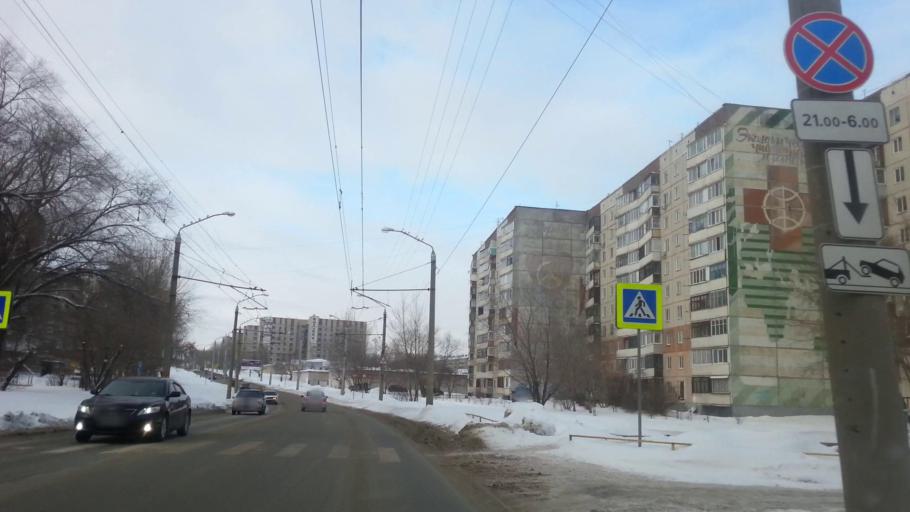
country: RU
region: Altai Krai
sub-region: Gorod Barnaulskiy
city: Barnaul
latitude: 53.3687
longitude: 83.7041
